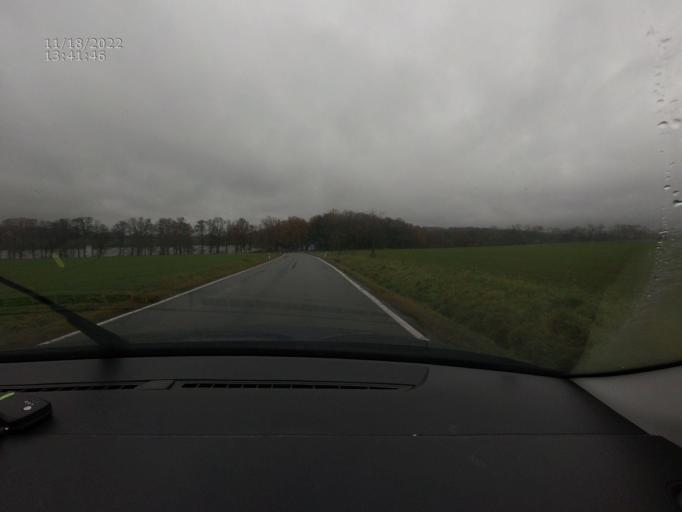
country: CZ
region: Plzensky
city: Kasejovice
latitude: 49.4336
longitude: 13.7896
